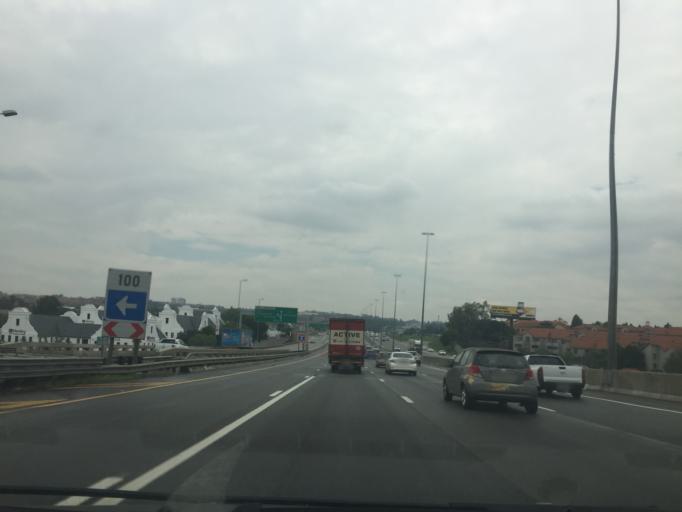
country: ZA
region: Gauteng
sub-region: City of Johannesburg Metropolitan Municipality
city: Midrand
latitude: -26.0380
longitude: 28.0543
